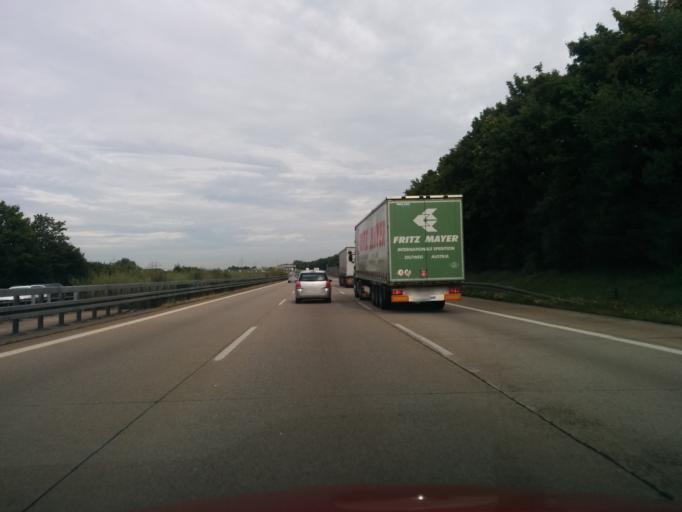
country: DE
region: Baden-Wuerttemberg
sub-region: Regierungsbezirk Stuttgart
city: Denkendorf
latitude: 48.6880
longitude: 9.3171
